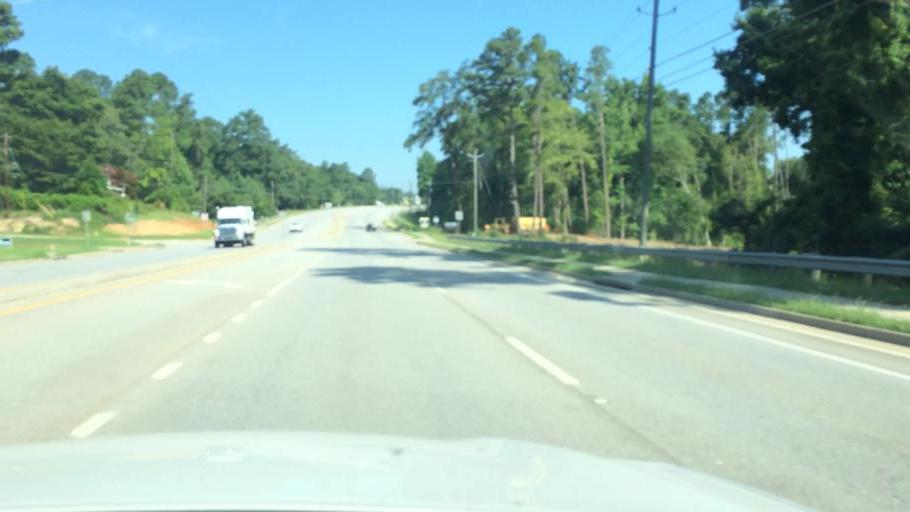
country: US
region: Georgia
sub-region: Columbia County
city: Martinez
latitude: 33.5223
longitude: -82.0659
